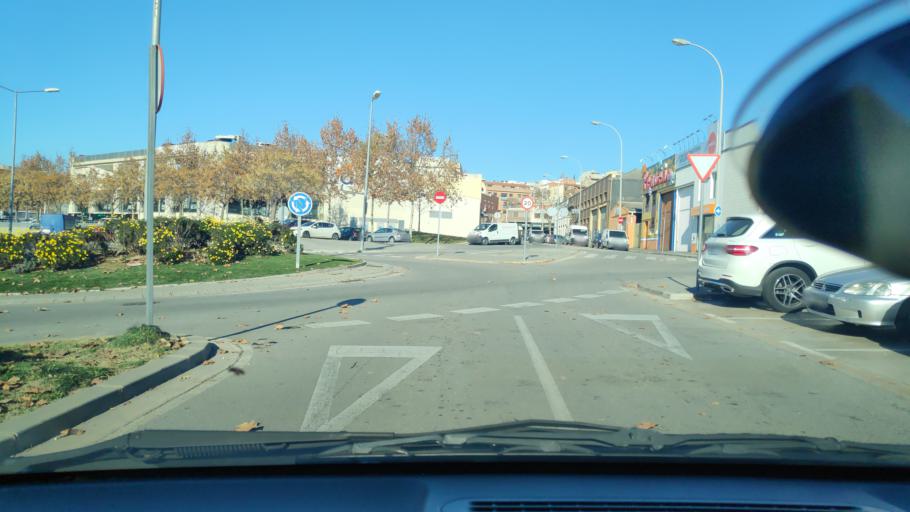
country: ES
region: Catalonia
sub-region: Provincia de Barcelona
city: Sant Quirze del Valles
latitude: 41.5451
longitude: 2.0920
